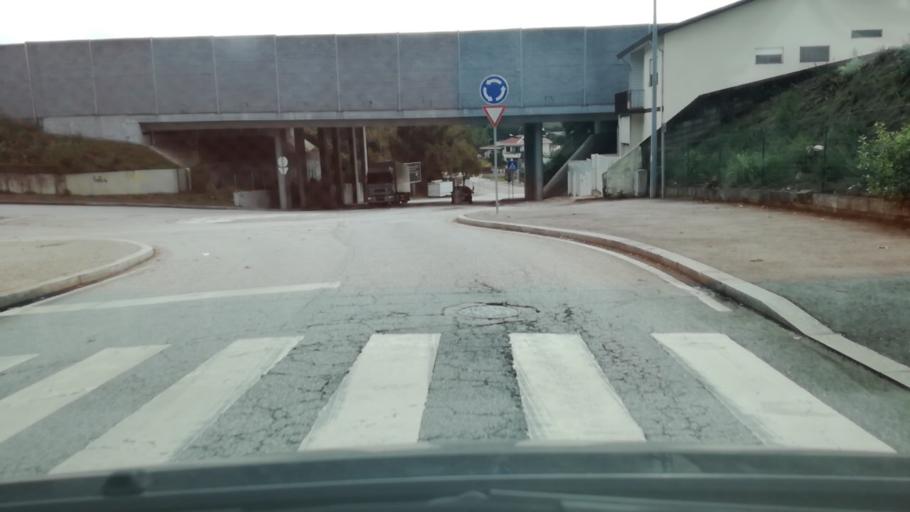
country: PT
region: Porto
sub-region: Maia
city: Maia
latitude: 41.2406
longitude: -8.6339
